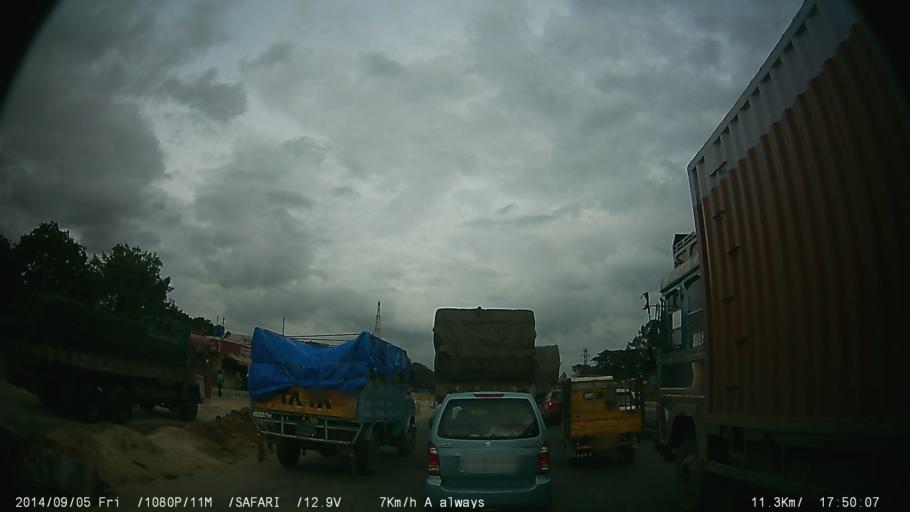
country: IN
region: Tamil Nadu
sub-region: Krishnagiri
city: Hosur
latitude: 12.7631
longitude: 77.7936
